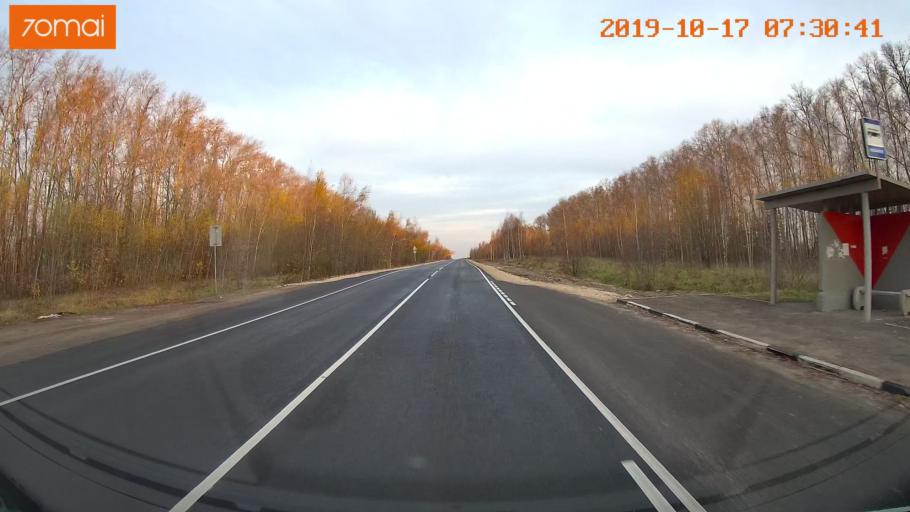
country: RU
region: Ivanovo
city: Gavrilov Posad
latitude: 56.3795
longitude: 40.0068
